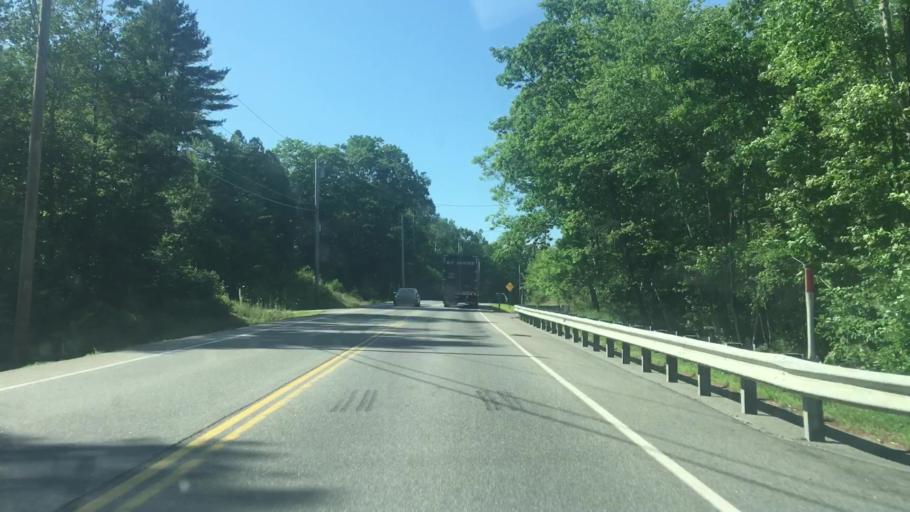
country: US
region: Maine
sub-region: York County
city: Buxton
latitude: 43.5798
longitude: -70.5167
